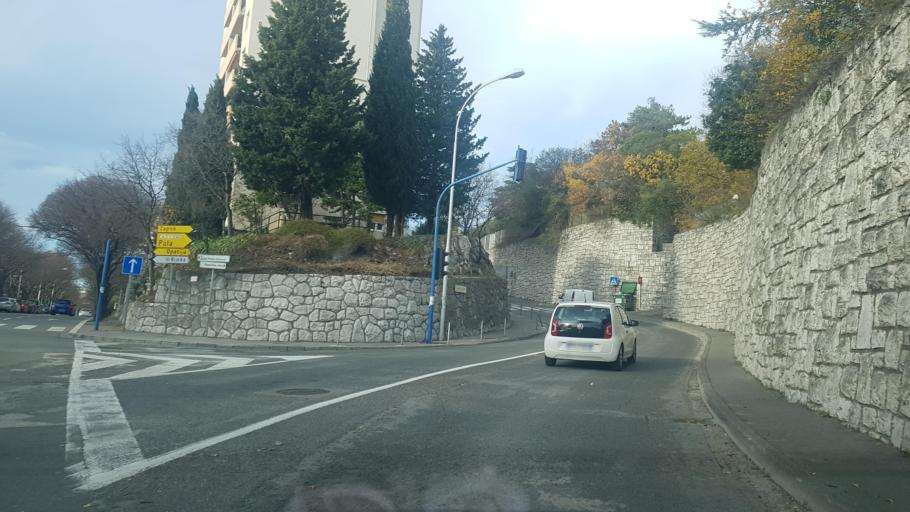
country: HR
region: Primorsko-Goranska
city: Cavle
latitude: 45.3151
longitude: 14.4722
